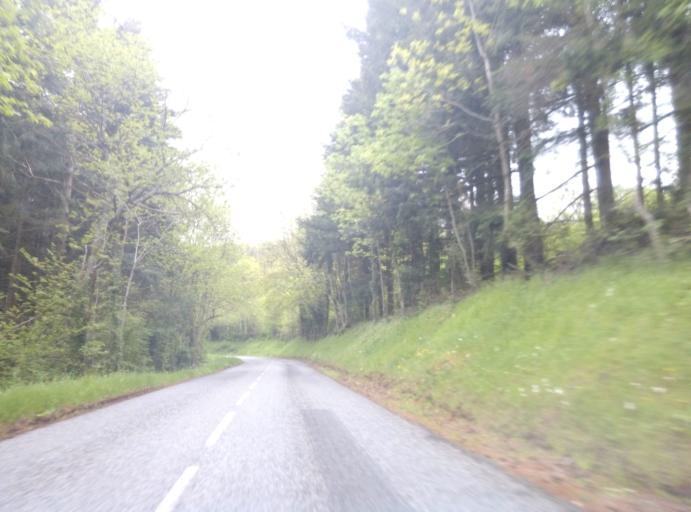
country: FR
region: Rhone-Alpes
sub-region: Departement du Rhone
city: Tarare
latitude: 45.9212
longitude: 4.4292
